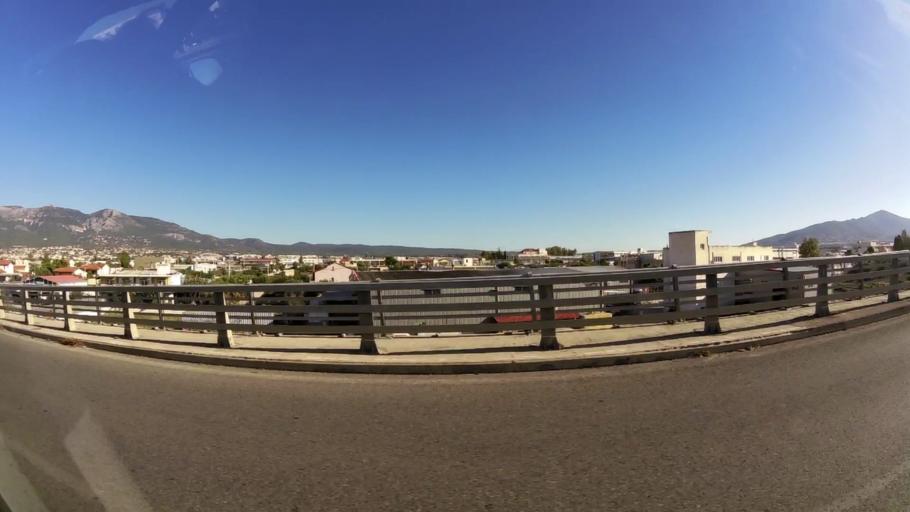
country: GR
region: Attica
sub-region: Nomarchia Athinas
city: Metamorfosi
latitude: 38.0882
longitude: 23.7608
